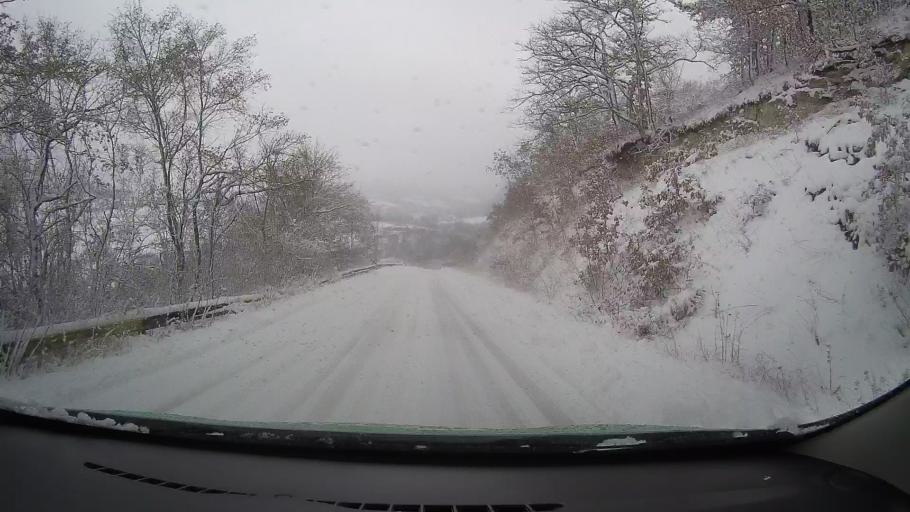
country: RO
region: Hunedoara
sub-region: Comuna Carjiti
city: Carjiti
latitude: 45.8393
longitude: 22.8386
